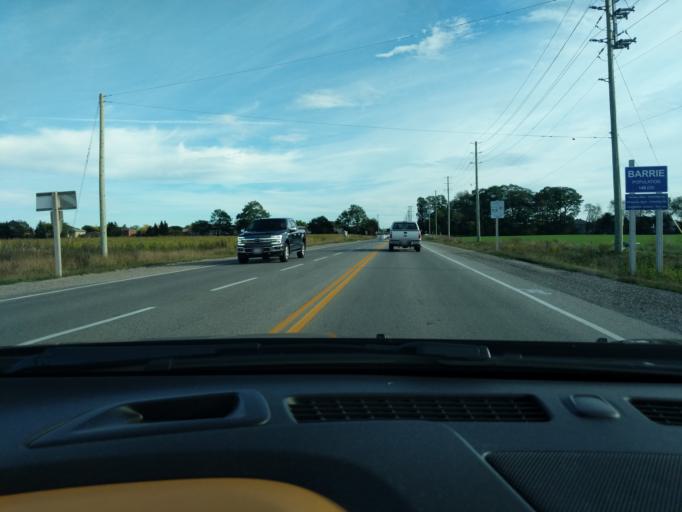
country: CA
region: Ontario
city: Barrie
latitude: 44.3987
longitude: -79.7399
